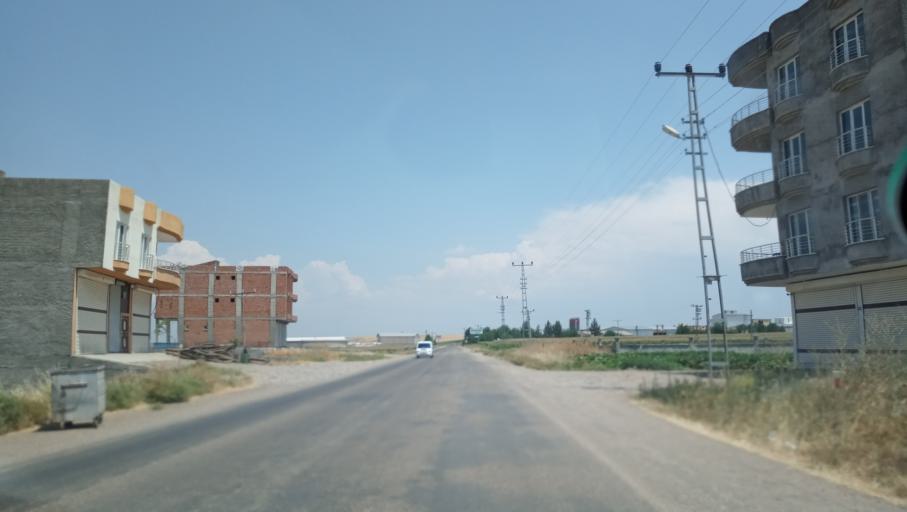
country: TR
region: Diyarbakir
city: Aralik
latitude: 37.8273
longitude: 40.6794
